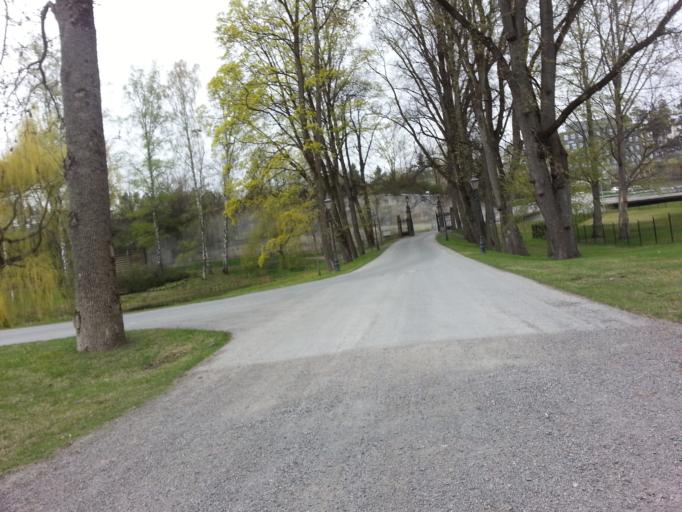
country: NO
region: Akershus
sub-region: Baerum
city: Lysaker
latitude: 59.9150
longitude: 10.6559
